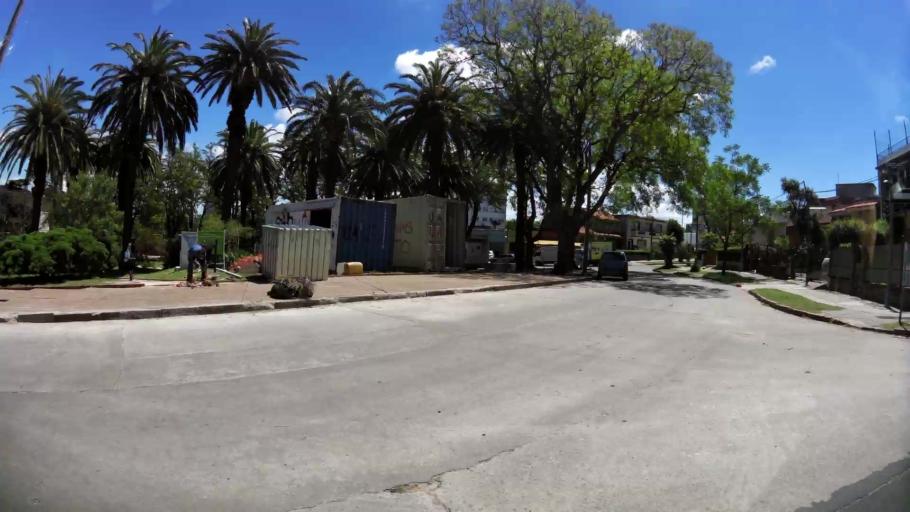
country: UY
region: Canelones
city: Paso de Carrasco
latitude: -34.8941
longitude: -56.1149
